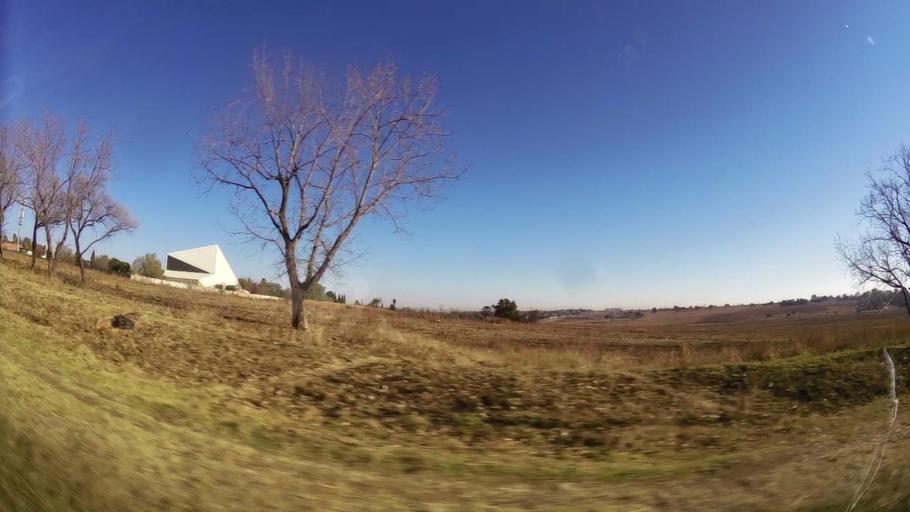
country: ZA
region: Gauteng
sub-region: Ekurhuleni Metropolitan Municipality
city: Tembisa
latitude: -26.0462
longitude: 28.2433
